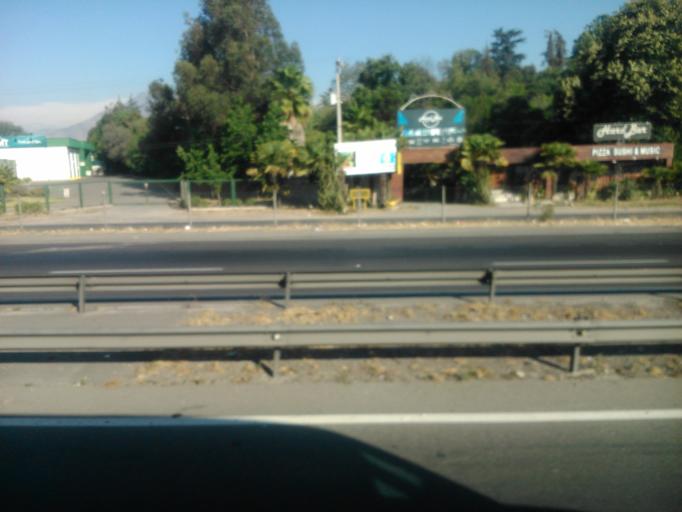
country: CL
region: Santiago Metropolitan
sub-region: Provincia de Maipo
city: Buin
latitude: -33.7283
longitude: -70.7314
